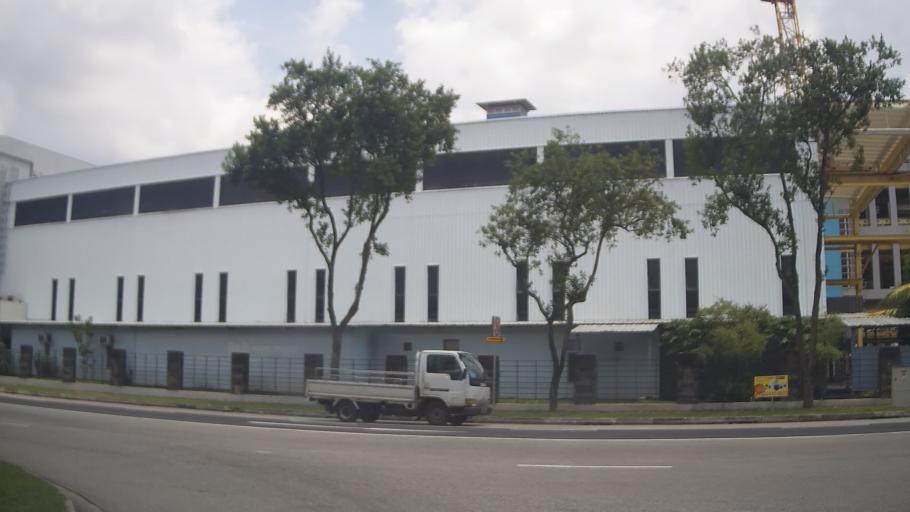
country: MY
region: Johor
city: Johor Bahru
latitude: 1.4552
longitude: 103.7998
